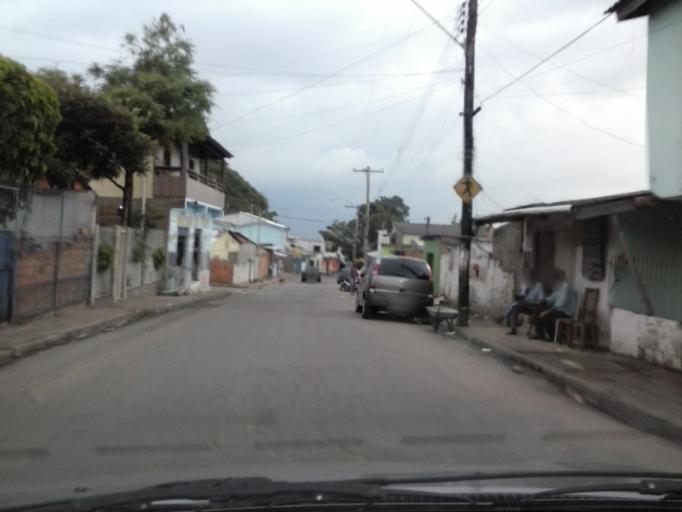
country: BR
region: Rio Grande do Sul
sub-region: Porto Alegre
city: Porto Alegre
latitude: -30.0500
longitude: -51.1527
